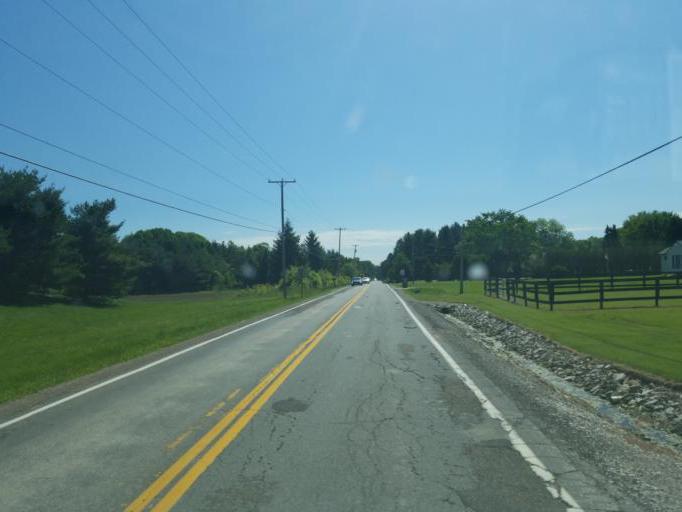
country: US
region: Ohio
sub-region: Summit County
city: Twinsburg
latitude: 41.2846
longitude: -81.4341
